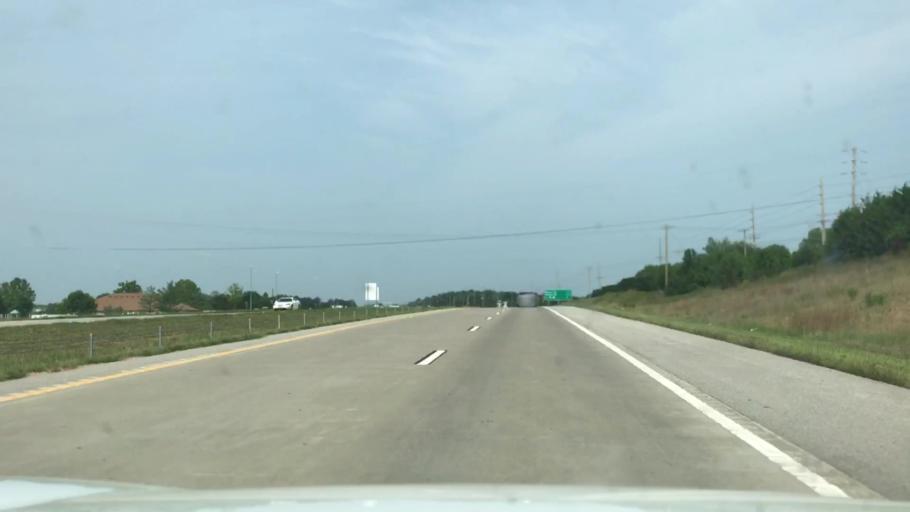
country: US
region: Missouri
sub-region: Saint Charles County
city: Dardenne Prairie
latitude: 38.7584
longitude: -90.7121
